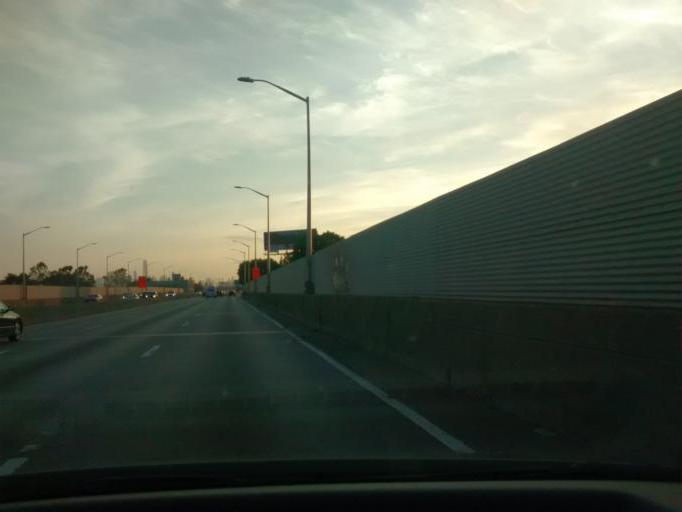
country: US
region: New York
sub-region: Queens County
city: Long Island City
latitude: 40.7358
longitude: -73.9147
